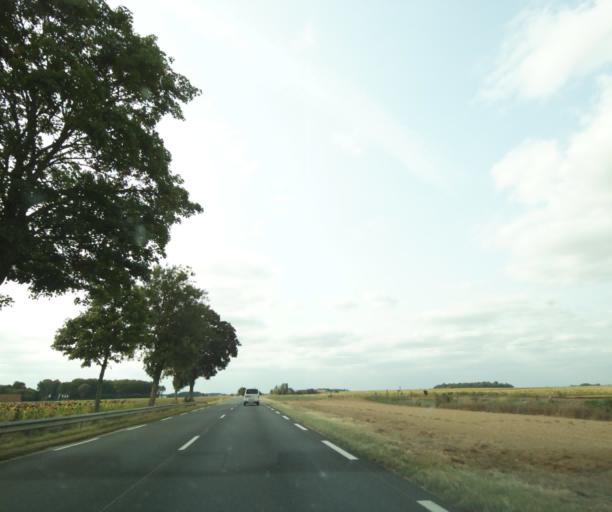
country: FR
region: Centre
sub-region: Departement d'Indre-et-Loire
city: Truyes
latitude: 47.2404
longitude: 0.8633
